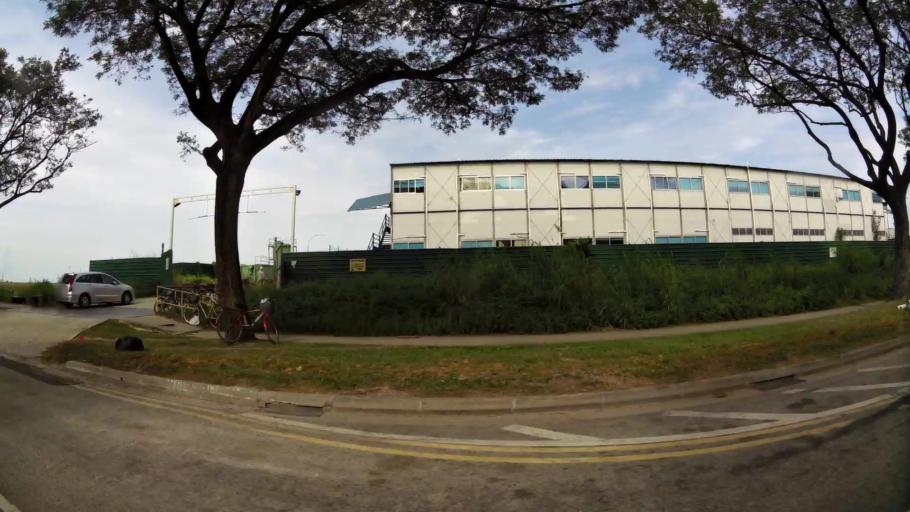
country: MY
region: Johor
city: Johor Bahru
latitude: 1.3189
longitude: 103.6287
